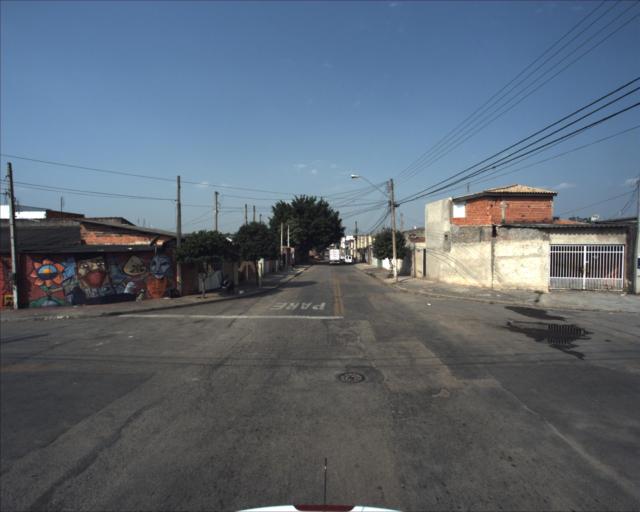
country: BR
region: Sao Paulo
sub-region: Sorocaba
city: Sorocaba
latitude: -23.4330
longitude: -47.4539
